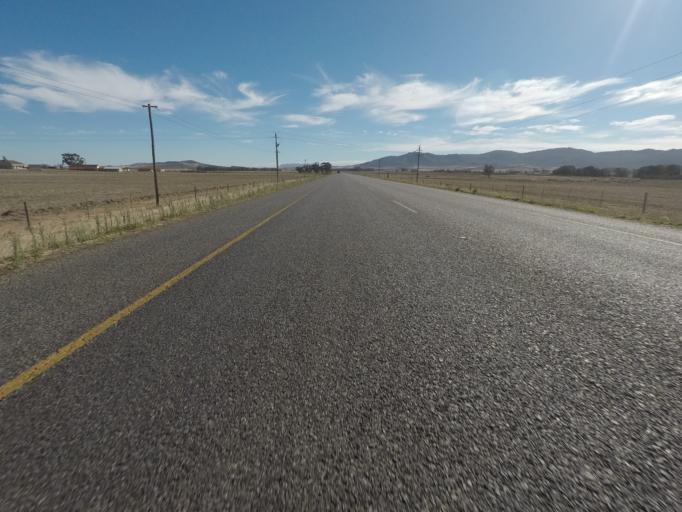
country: ZA
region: Western Cape
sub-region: West Coast District Municipality
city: Malmesbury
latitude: -33.6369
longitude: 18.7186
